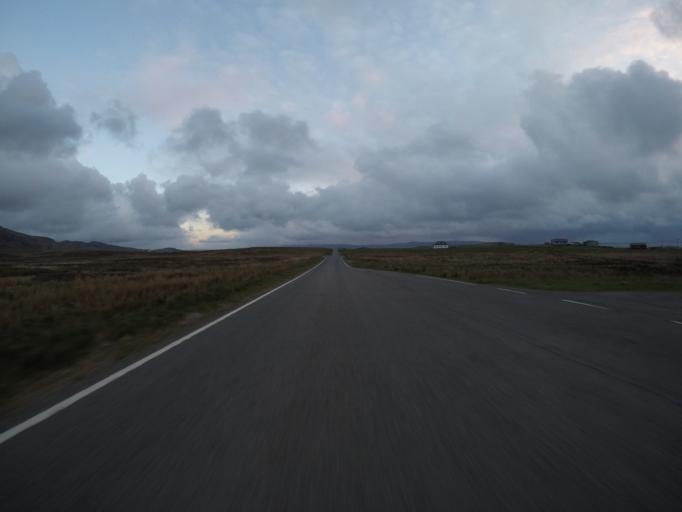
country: GB
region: Scotland
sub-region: Highland
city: Portree
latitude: 57.6569
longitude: -6.3756
